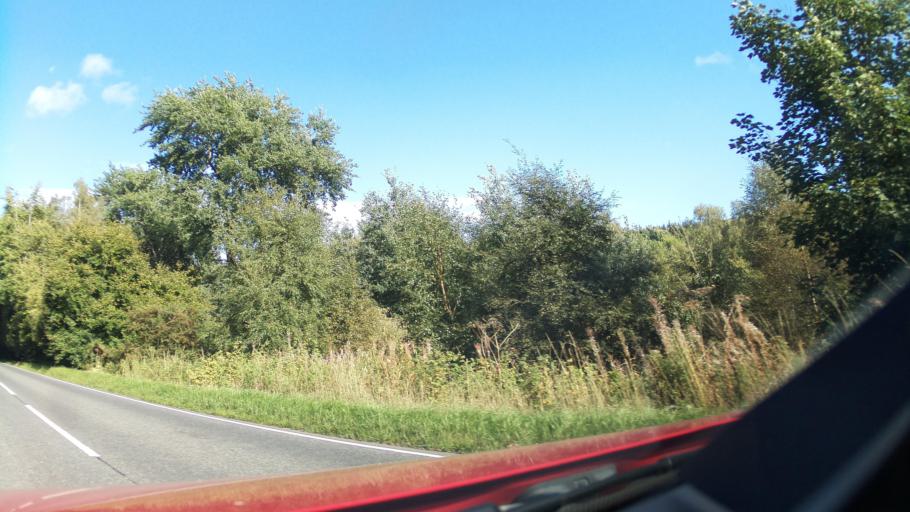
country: GB
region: Scotland
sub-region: The Scottish Borders
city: West Linton
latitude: 55.7019
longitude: -3.3633
